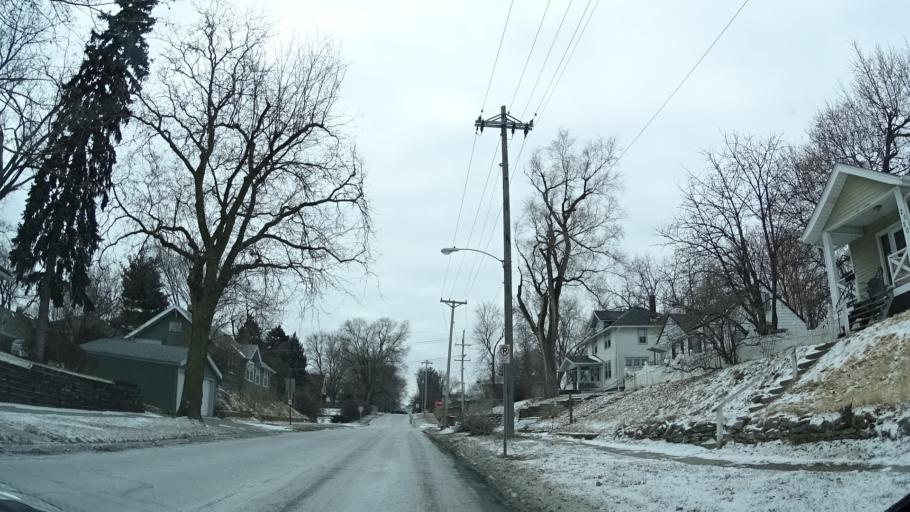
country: US
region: Nebraska
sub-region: Douglas County
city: Omaha
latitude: 41.2785
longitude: -96.0048
